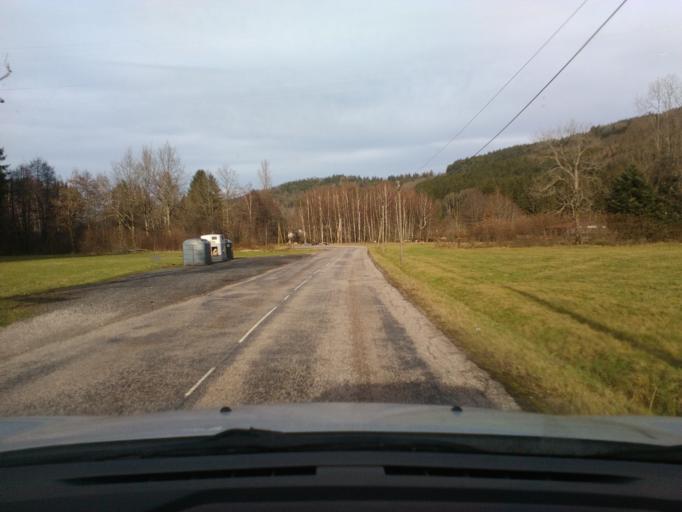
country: FR
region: Lorraine
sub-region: Departement des Vosges
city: Fraize
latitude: 48.1533
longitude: 6.9846
